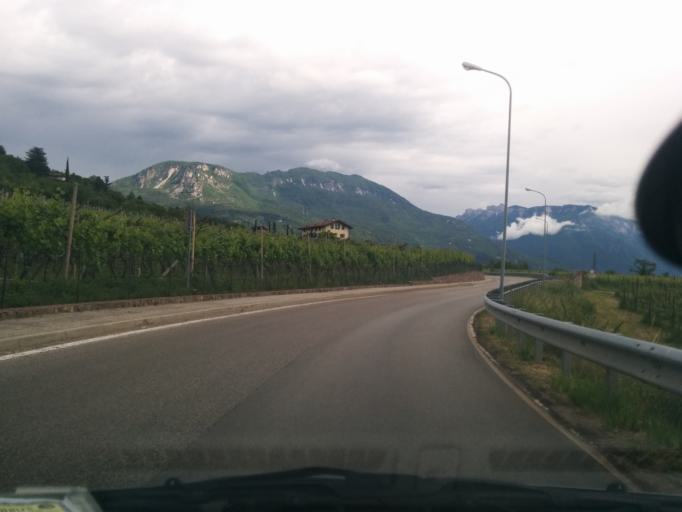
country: IT
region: Trentino-Alto Adige
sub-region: Provincia di Trento
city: Trento
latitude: 46.0854
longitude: 11.1338
